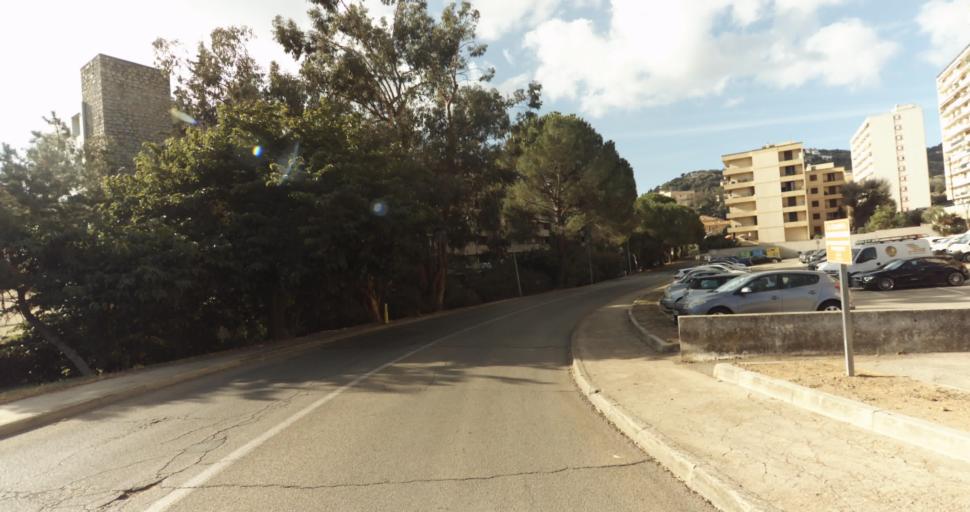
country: FR
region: Corsica
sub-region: Departement de la Corse-du-Sud
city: Ajaccio
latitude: 41.9326
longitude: 8.7341
